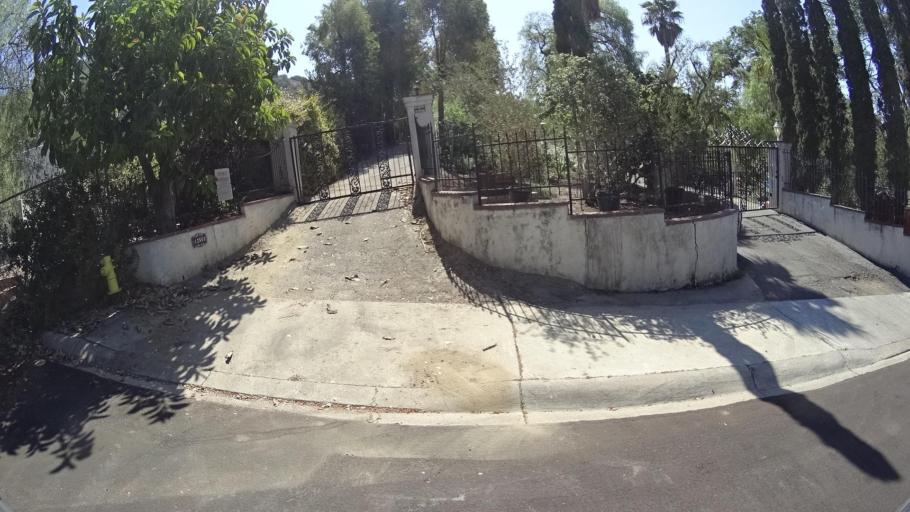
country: US
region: California
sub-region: Orange County
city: North Tustin
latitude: 33.7806
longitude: -117.7862
